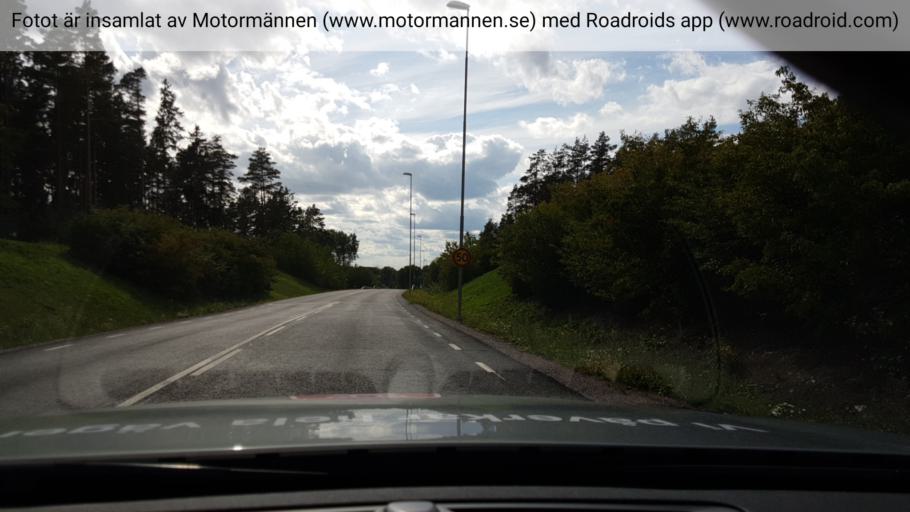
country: SE
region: Stockholm
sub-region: Upplands-Bro Kommun
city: Bro
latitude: 59.5093
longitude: 17.6690
